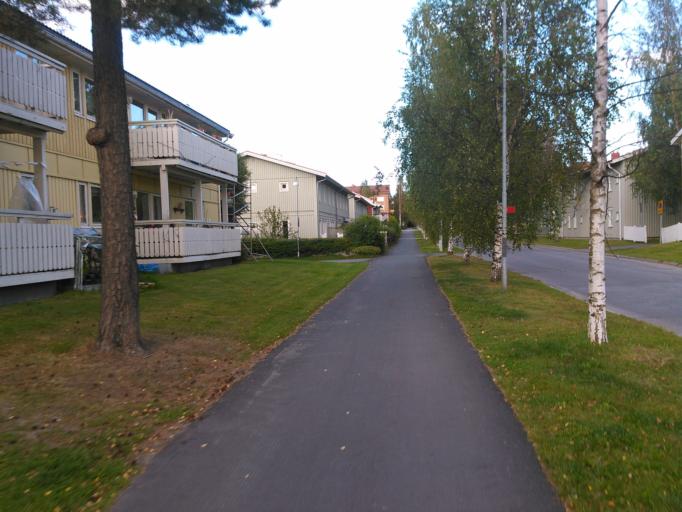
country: SE
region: Vaesterbotten
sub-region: Umea Kommun
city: Ersmark
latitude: 63.8079
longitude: 20.3385
